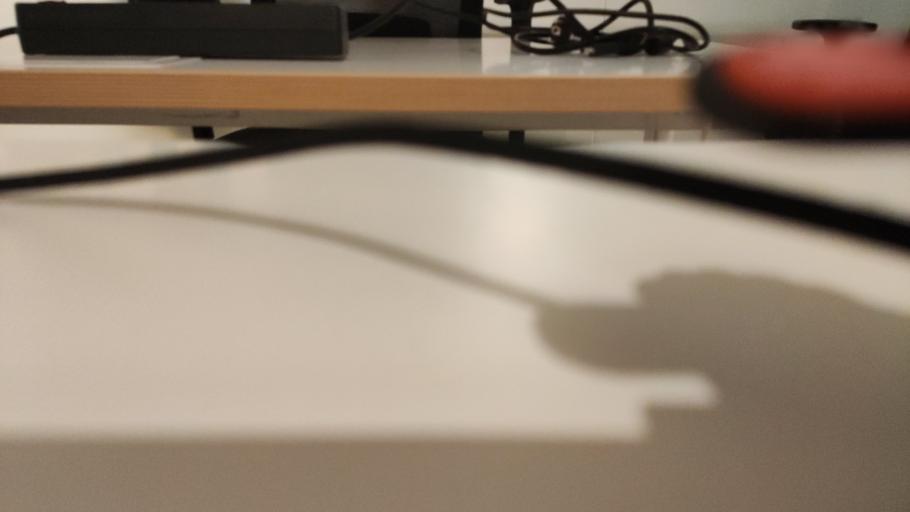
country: RU
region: Moskovskaya
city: Proletarskiy
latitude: 54.9758
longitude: 37.4103
